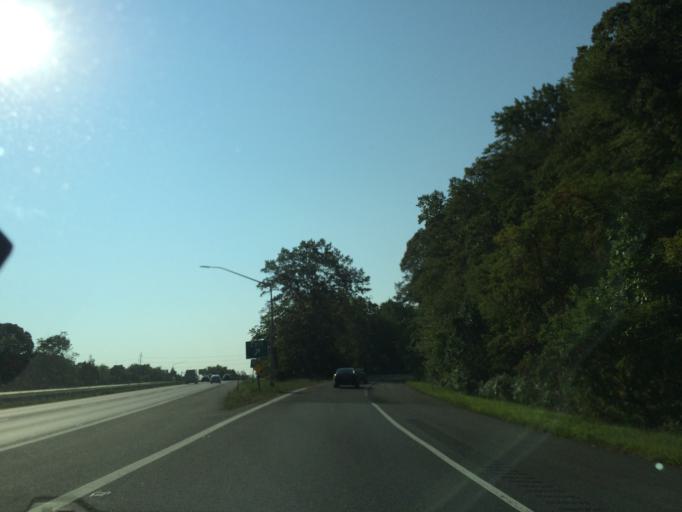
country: US
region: Maryland
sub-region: Anne Arundel County
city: Gambrills
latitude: 39.0681
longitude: -76.6497
